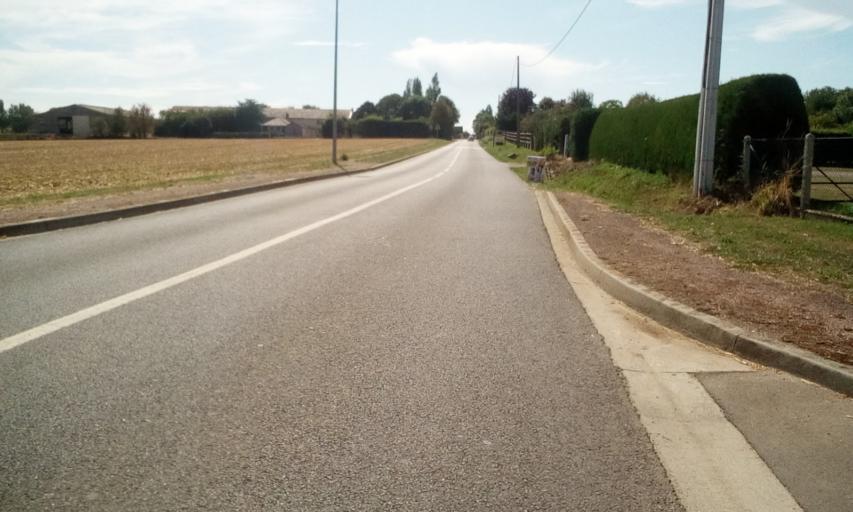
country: FR
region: Lower Normandy
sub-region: Departement du Calvados
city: Eterville
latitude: 49.1341
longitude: -0.4136
